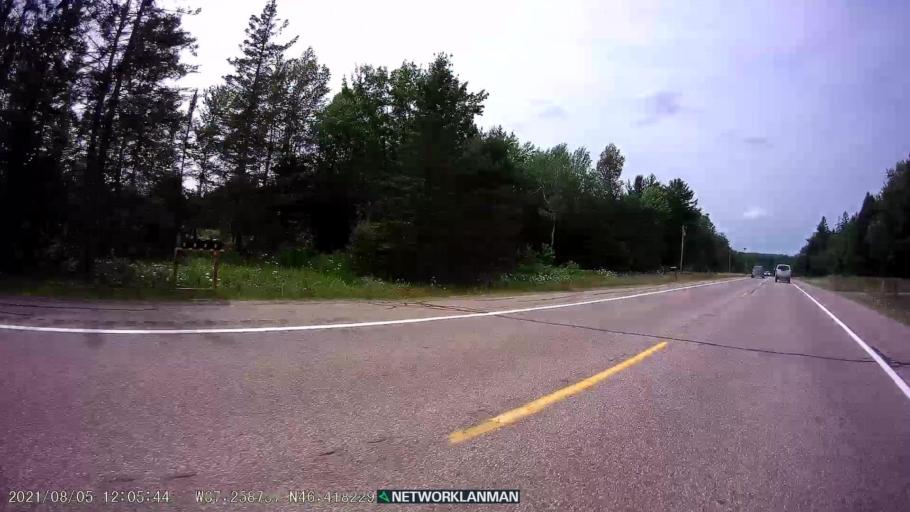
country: US
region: Michigan
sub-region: Marquette County
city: Harvey
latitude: 46.4184
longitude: -87.2591
